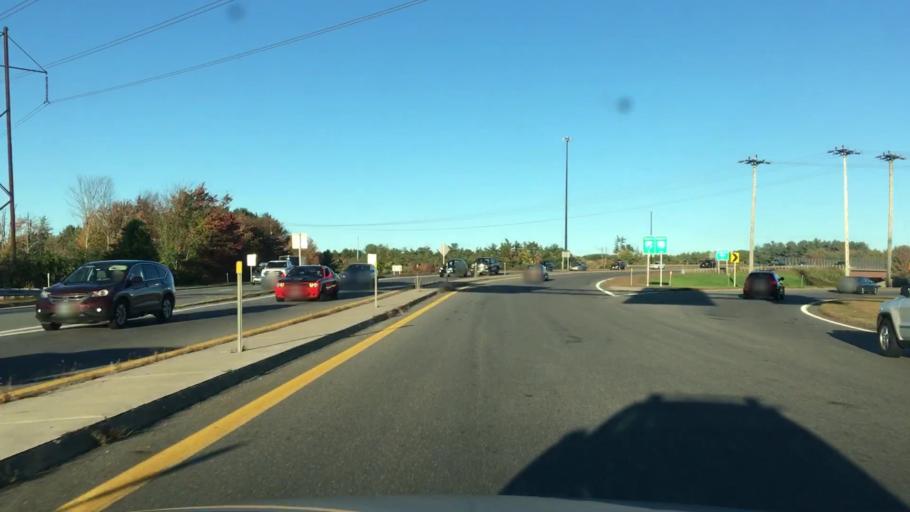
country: US
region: New Hampshire
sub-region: Rockingham County
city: North Hampton
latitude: 42.9650
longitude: -70.8590
